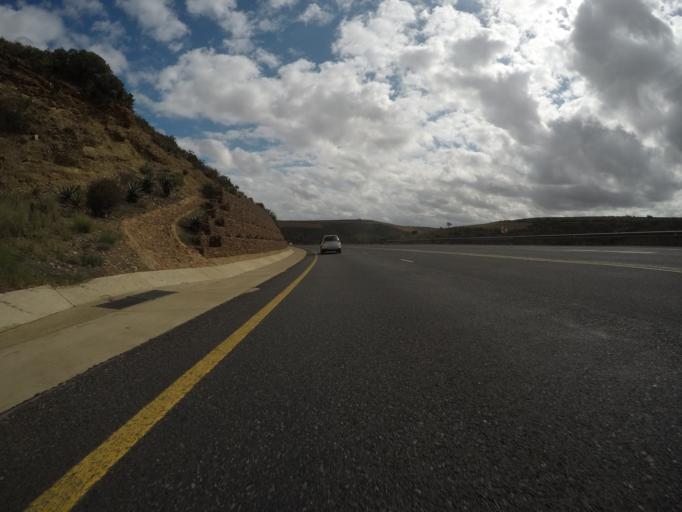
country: ZA
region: Western Cape
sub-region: Eden District Municipality
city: Riversdale
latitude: -34.1460
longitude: 21.2858
